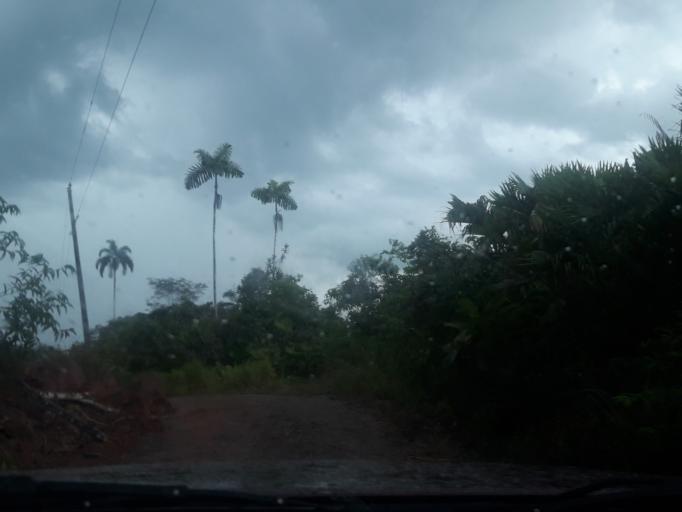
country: EC
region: Napo
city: Tena
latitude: -1.0869
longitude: -77.7078
